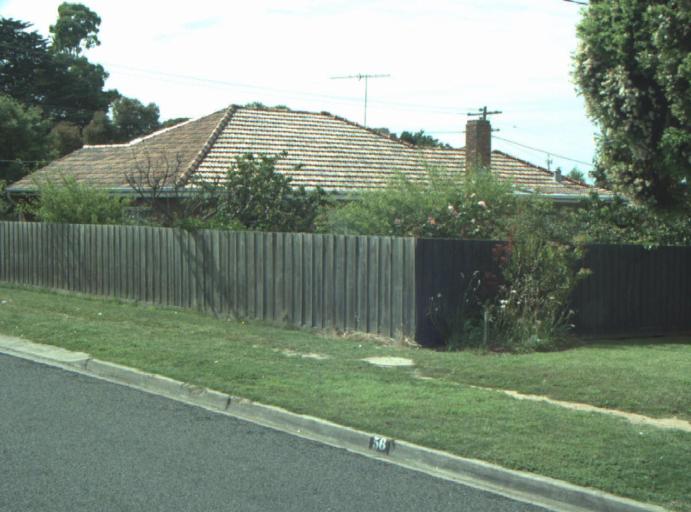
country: AU
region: Victoria
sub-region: Greater Geelong
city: Clifton Springs
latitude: -38.1686
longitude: 144.5710
